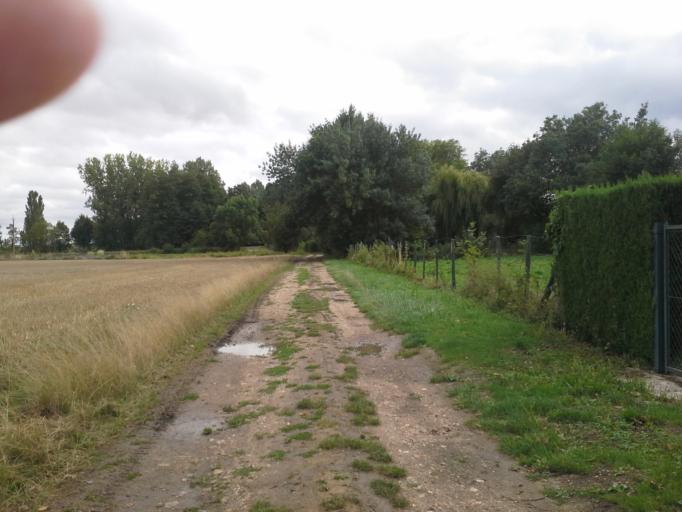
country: FR
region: Centre
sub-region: Departement du Loir-et-Cher
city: Villiers-sur-Loir
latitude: 47.8051
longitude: 0.9794
